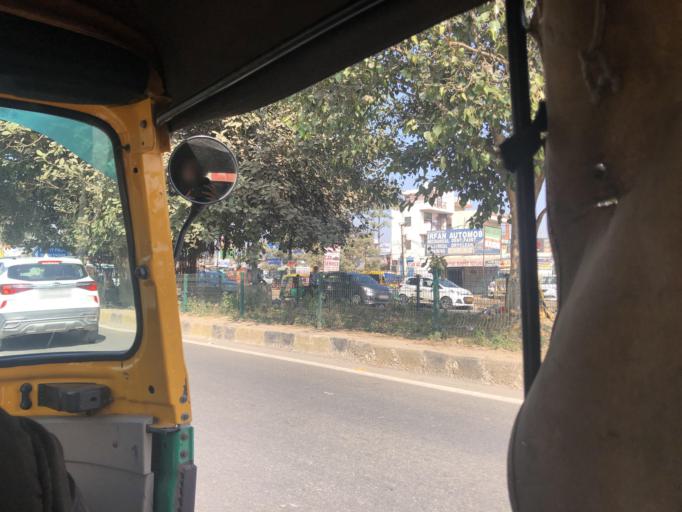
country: IN
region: Haryana
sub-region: Gurgaon
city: Gurgaon
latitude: 28.4390
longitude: 77.0890
